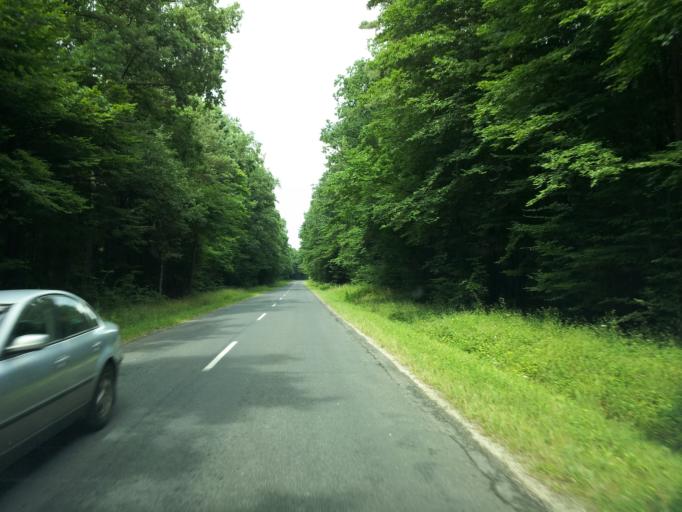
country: HU
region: Zala
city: Turje
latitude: 47.0716
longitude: 17.0176
